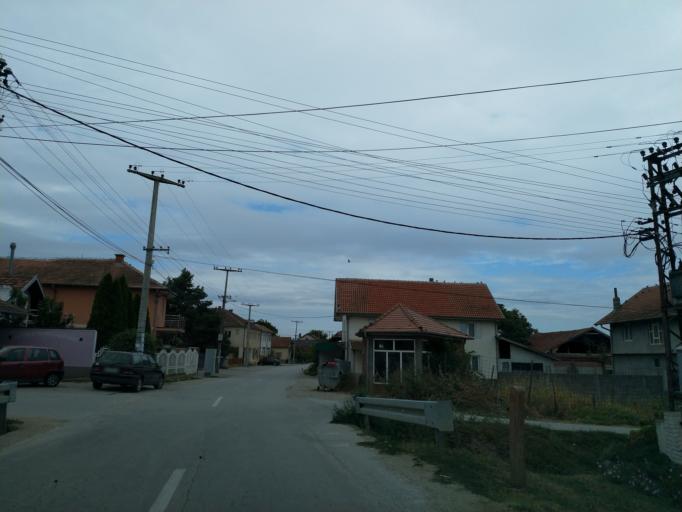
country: RS
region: Central Serbia
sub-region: Pomoravski Okrug
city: Cuprija
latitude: 43.8680
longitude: 21.3218
